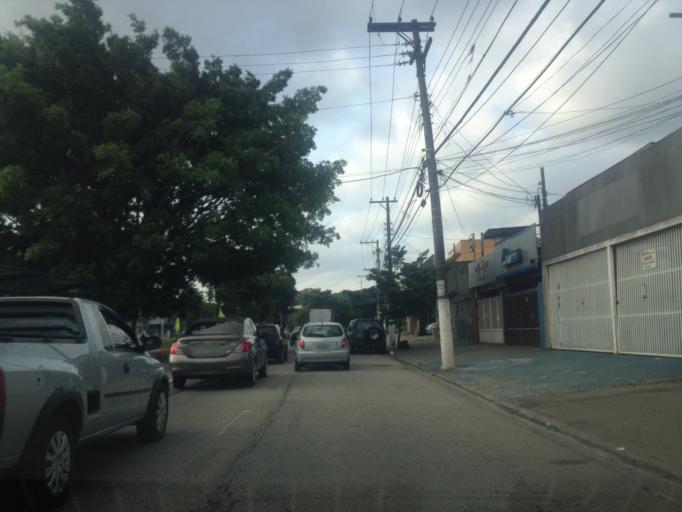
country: BR
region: Sao Paulo
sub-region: Diadema
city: Diadema
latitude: -23.6844
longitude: -46.7143
